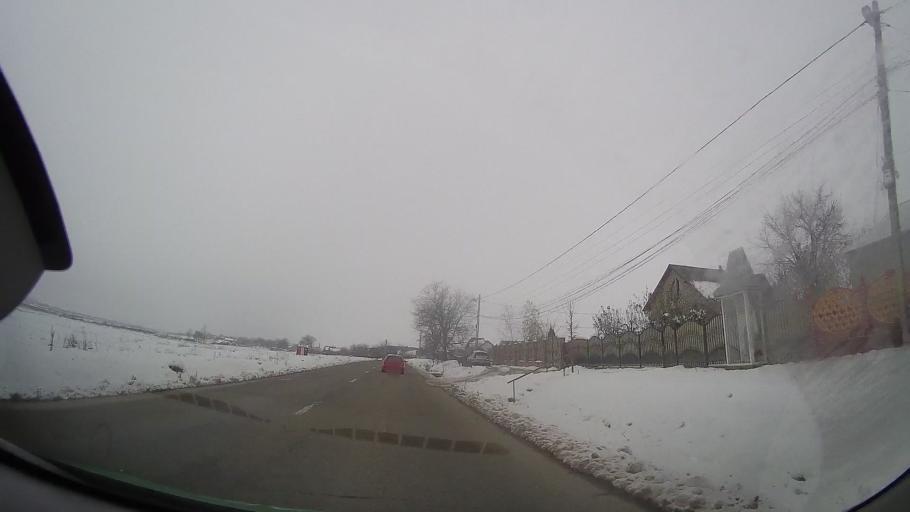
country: RO
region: Vaslui
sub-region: Comuna Negresti
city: Negresti
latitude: 46.8389
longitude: 27.4344
